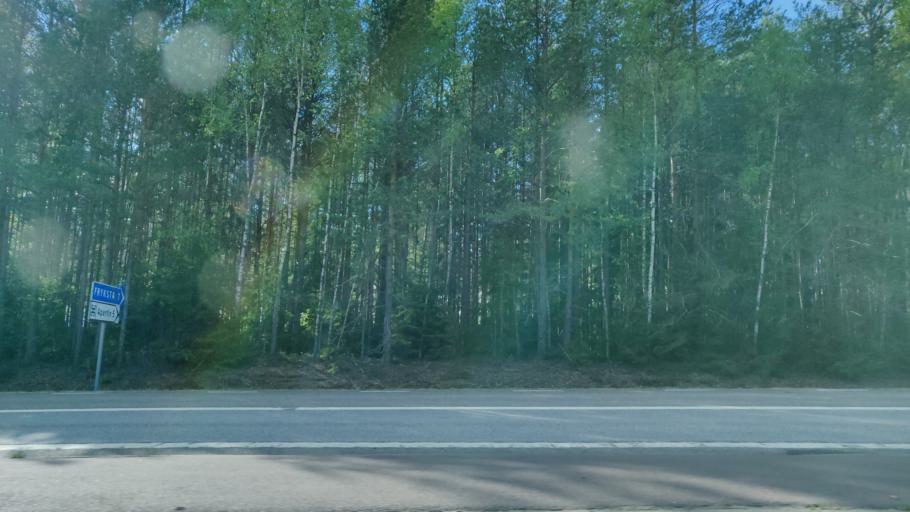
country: SE
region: Vaermland
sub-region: Forshaga Kommun
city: Forshaga
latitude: 59.4828
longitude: 13.4127
